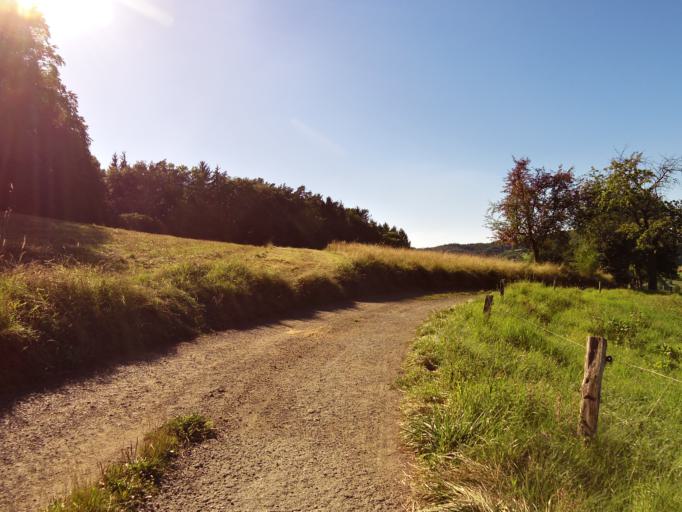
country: DE
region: Hesse
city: Reichelsheim
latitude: 49.6633
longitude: 8.8551
